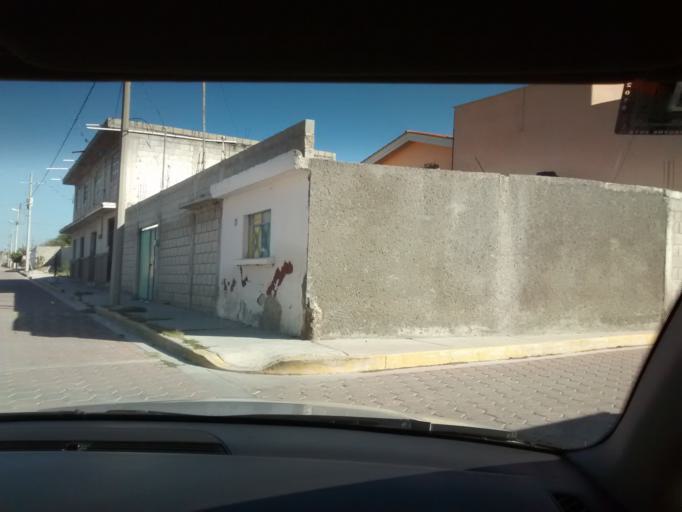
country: MX
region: Puebla
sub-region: Tepanco de Lopez
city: San Andres Cacaloapan
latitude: 18.5820
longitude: -97.5810
